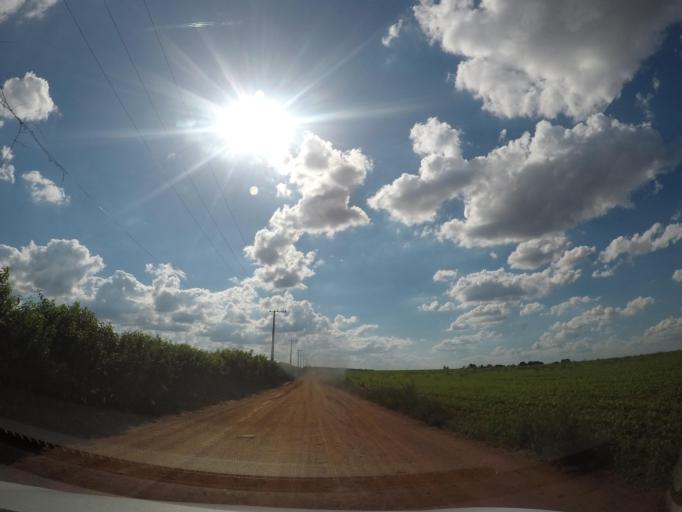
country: BR
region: Sao Paulo
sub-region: Sumare
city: Sumare
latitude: -22.8451
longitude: -47.3193
